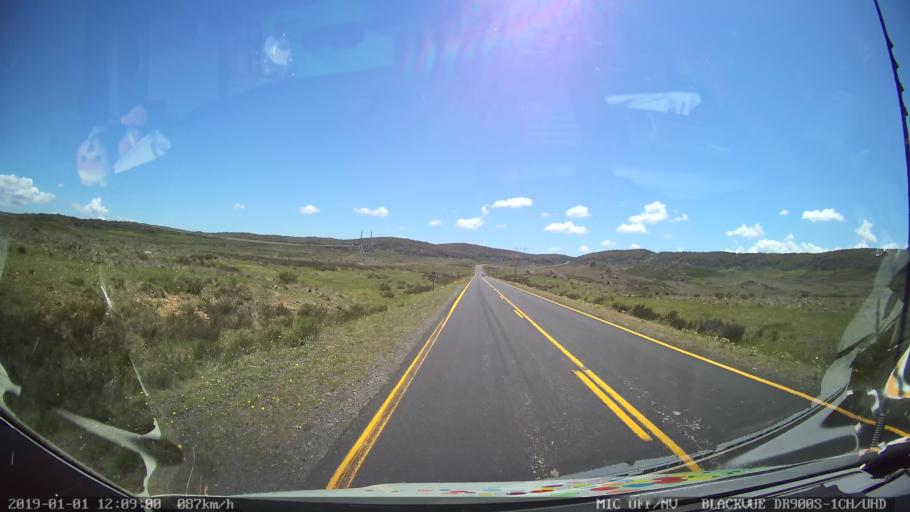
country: AU
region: New South Wales
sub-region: Tumut Shire
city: Tumut
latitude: -35.8130
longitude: 148.4963
